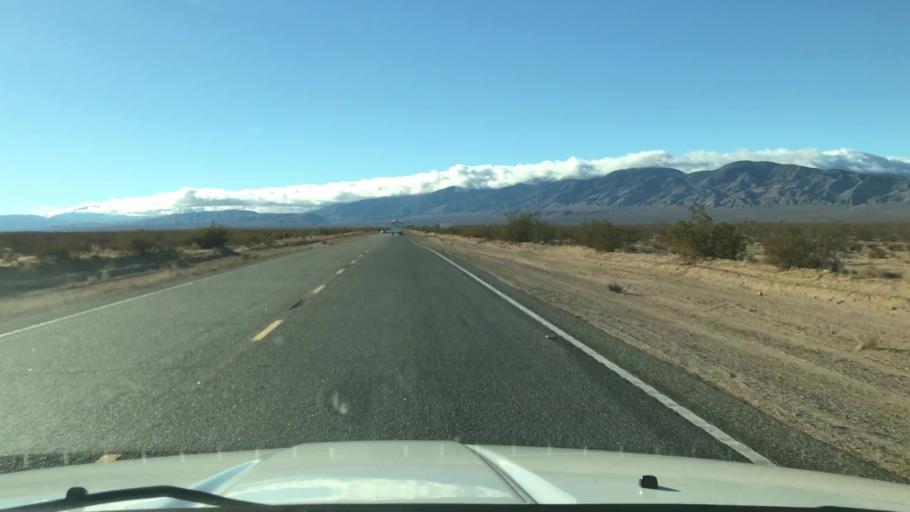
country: US
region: California
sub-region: Kern County
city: California City
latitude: 35.1252
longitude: -118.0633
